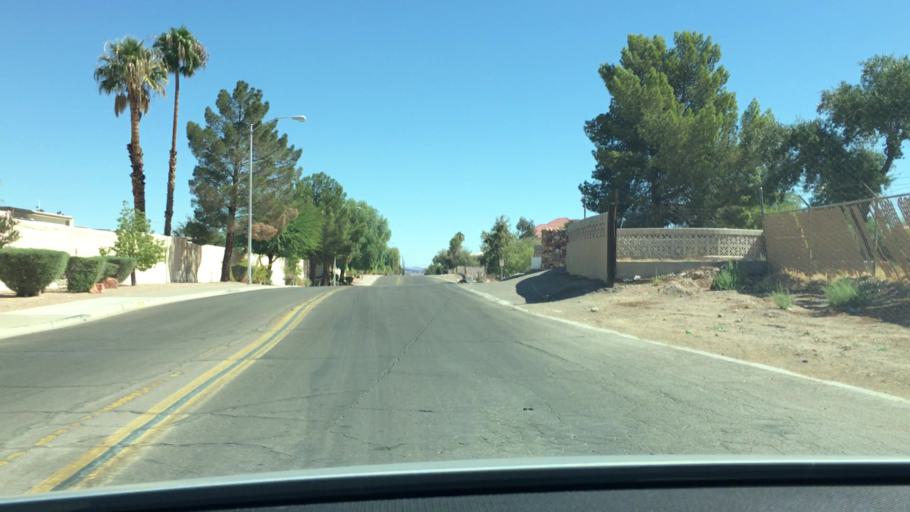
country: US
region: Nevada
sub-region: Clark County
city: Winchester
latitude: 36.1189
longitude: -115.0996
